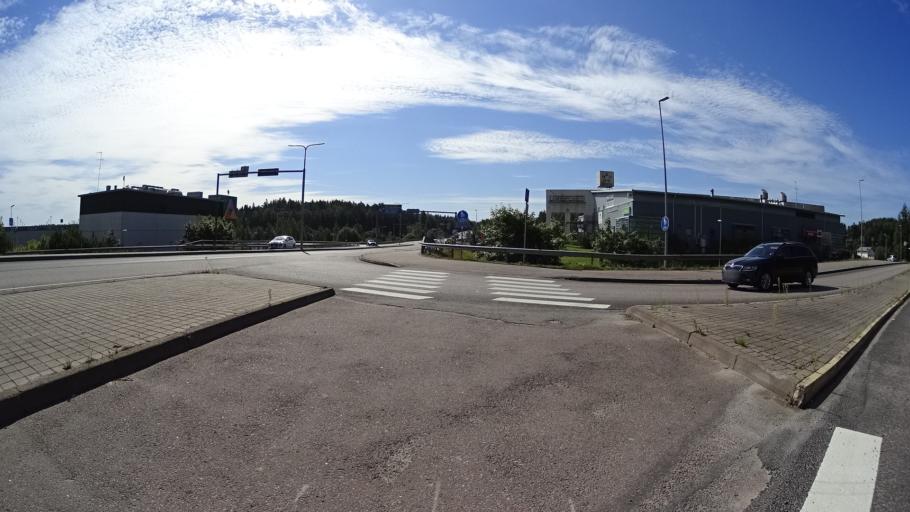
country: FI
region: Uusimaa
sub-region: Helsinki
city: Kirkkonummi
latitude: 60.1182
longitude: 24.4431
